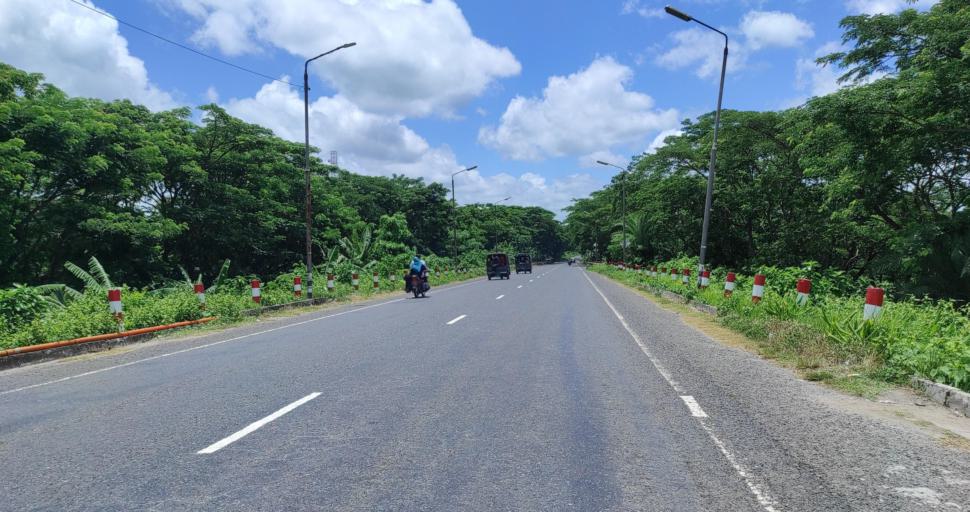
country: BD
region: Barisal
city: Gaurnadi
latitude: 22.8233
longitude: 90.2651
